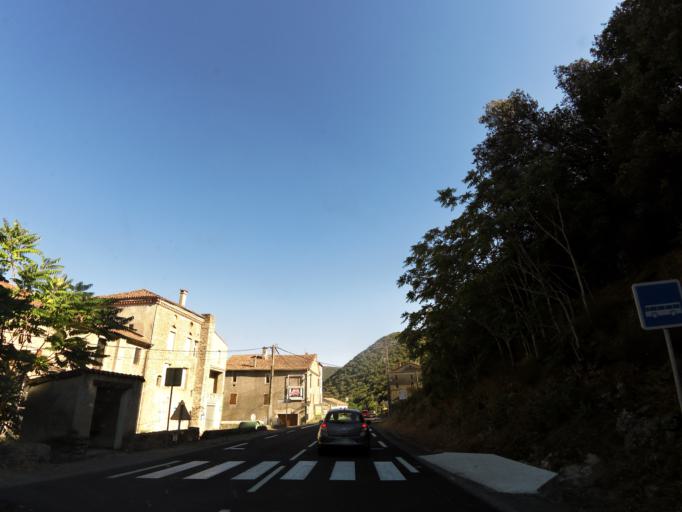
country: FR
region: Languedoc-Roussillon
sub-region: Departement du Gard
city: Valleraugue
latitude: 44.0334
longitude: 3.6778
